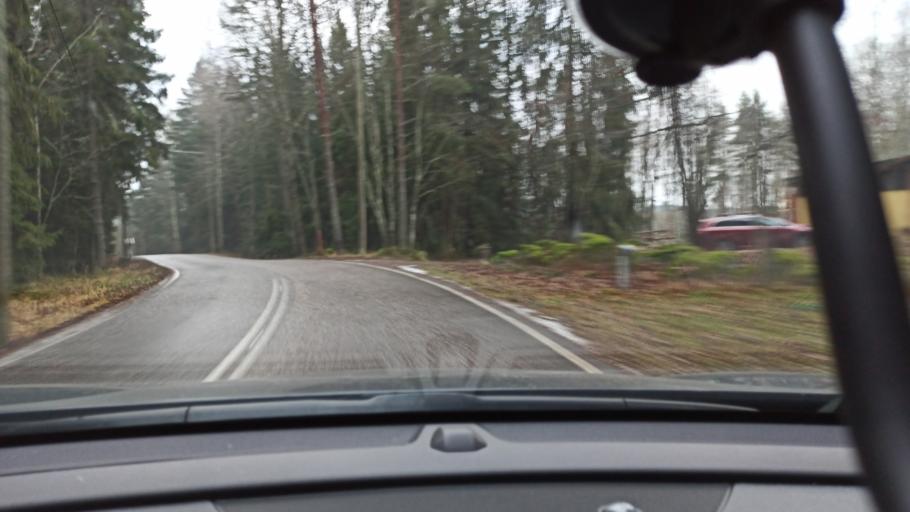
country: FI
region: Uusimaa
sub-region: Helsinki
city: Kirkkonummi
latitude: 60.1472
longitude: 24.4591
